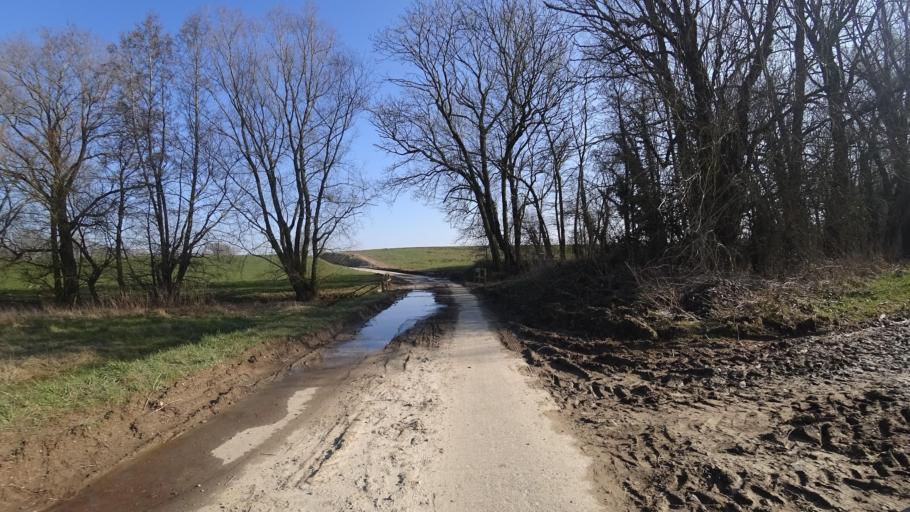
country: BE
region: Wallonia
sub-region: Province du Brabant Wallon
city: Chastre
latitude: 50.5712
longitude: 4.6453
